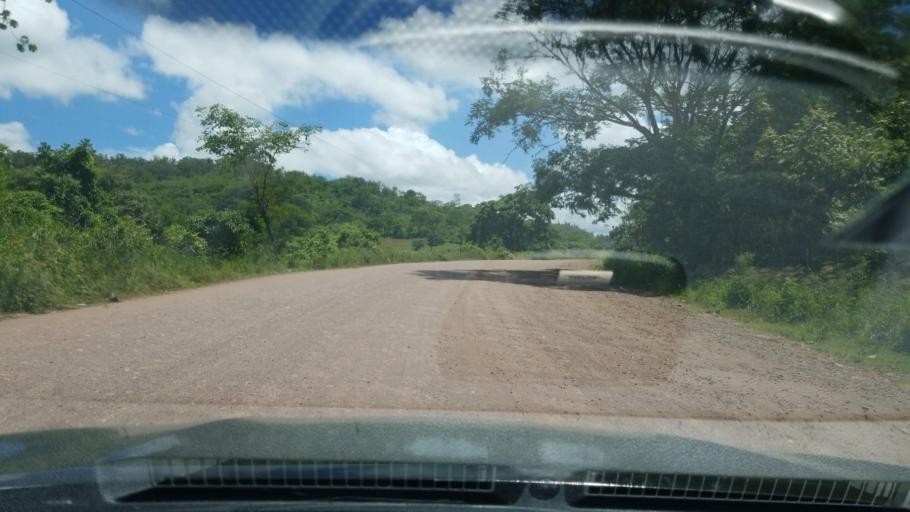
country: HN
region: Francisco Morazan
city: San Juan de Flores
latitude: 14.3229
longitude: -87.0470
